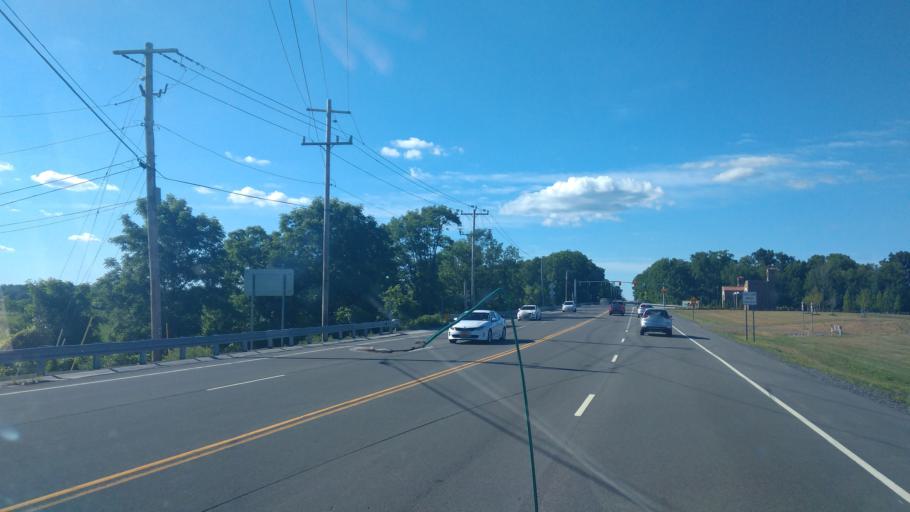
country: US
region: New York
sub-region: Seneca County
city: Waterloo
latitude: 42.9691
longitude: -76.8474
